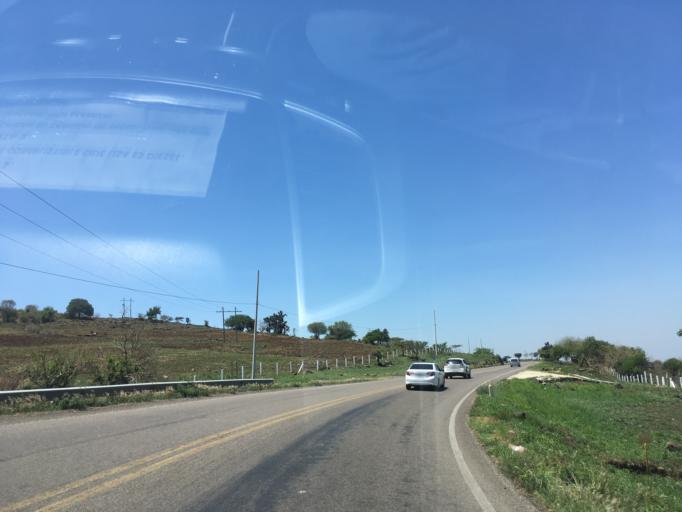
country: MX
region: Michoacan
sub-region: Tuxpan
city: La Soledad
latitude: 19.5201
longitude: -100.4717
